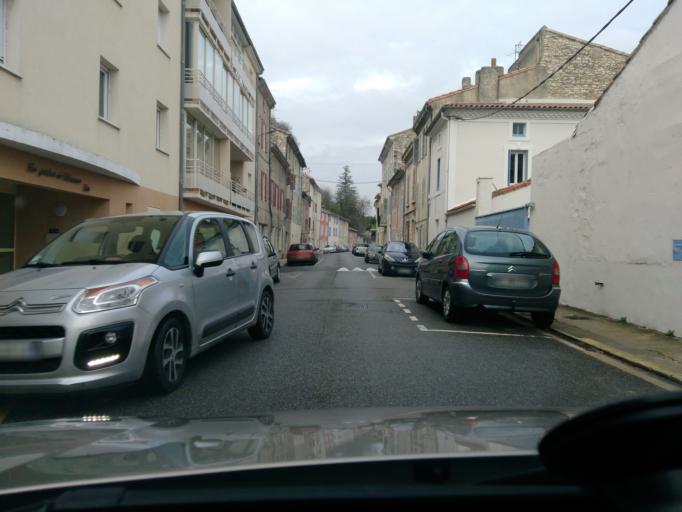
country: FR
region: Rhone-Alpes
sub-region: Departement de la Drome
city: Montelimar
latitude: 44.5593
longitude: 4.7562
